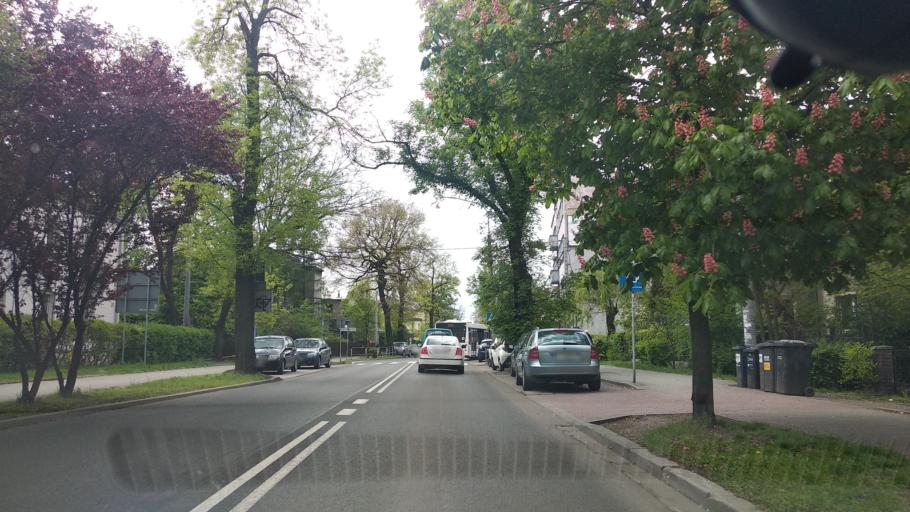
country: PL
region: Silesian Voivodeship
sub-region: Katowice
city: Katowice
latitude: 50.2257
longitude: 18.9689
